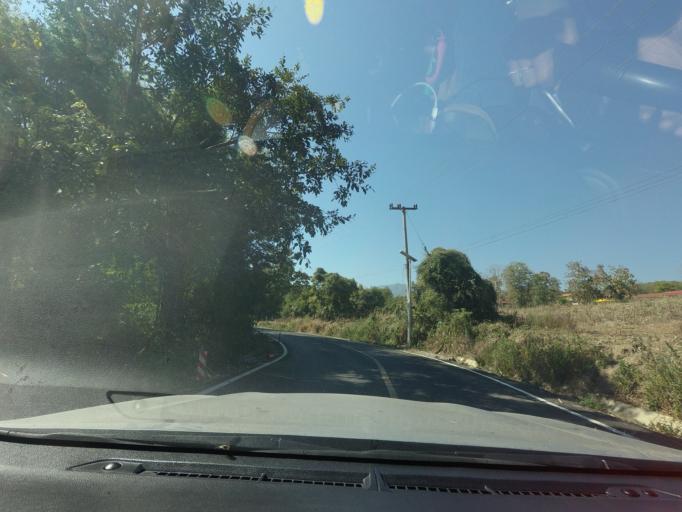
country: TH
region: Mae Hong Son
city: Wiang Nuea
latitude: 19.3790
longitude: 98.4346
